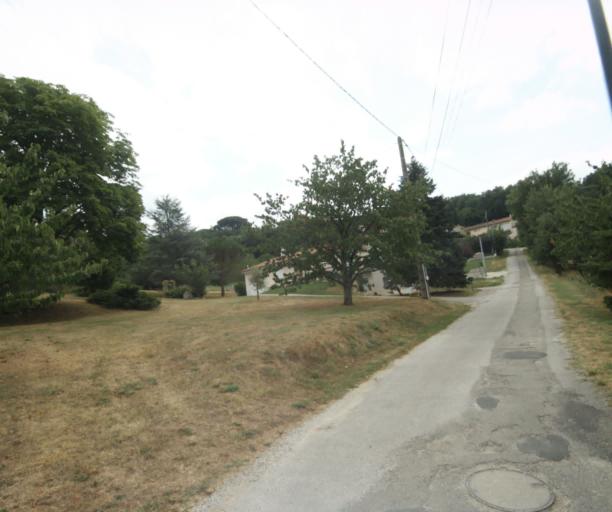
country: FR
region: Midi-Pyrenees
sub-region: Departement de la Haute-Garonne
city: Revel
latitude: 43.4468
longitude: 1.9986
